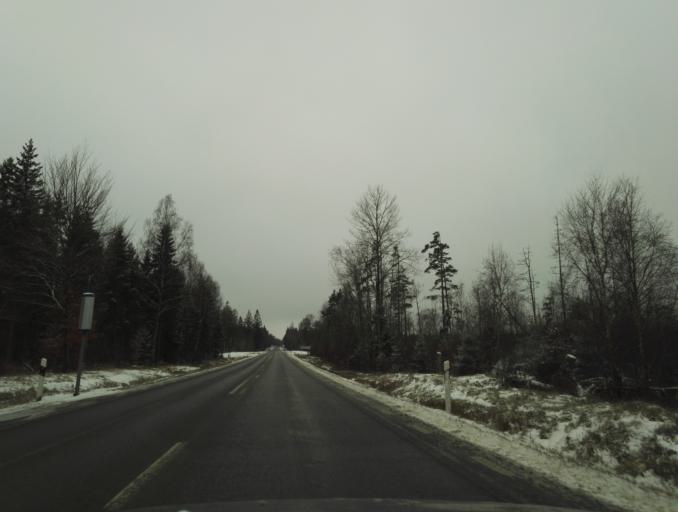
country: SE
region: Kronoberg
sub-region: Vaxjo Kommun
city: Gemla
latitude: 56.7973
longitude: 14.6377
